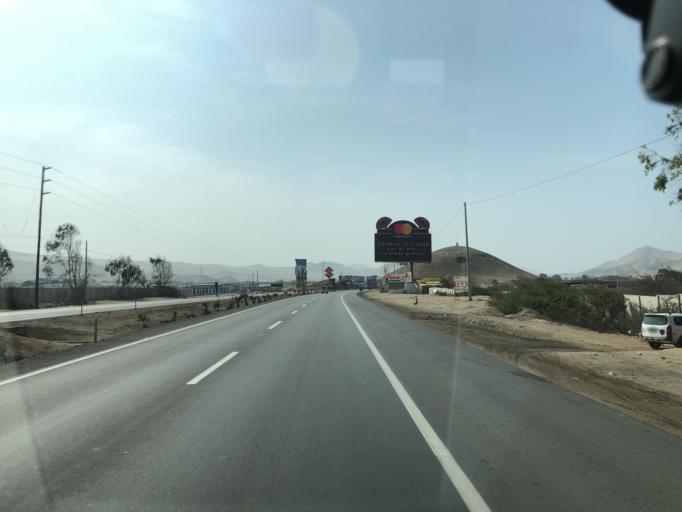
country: PE
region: Lima
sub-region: Provincia de Canete
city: Chilca
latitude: -12.5203
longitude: -76.7281
